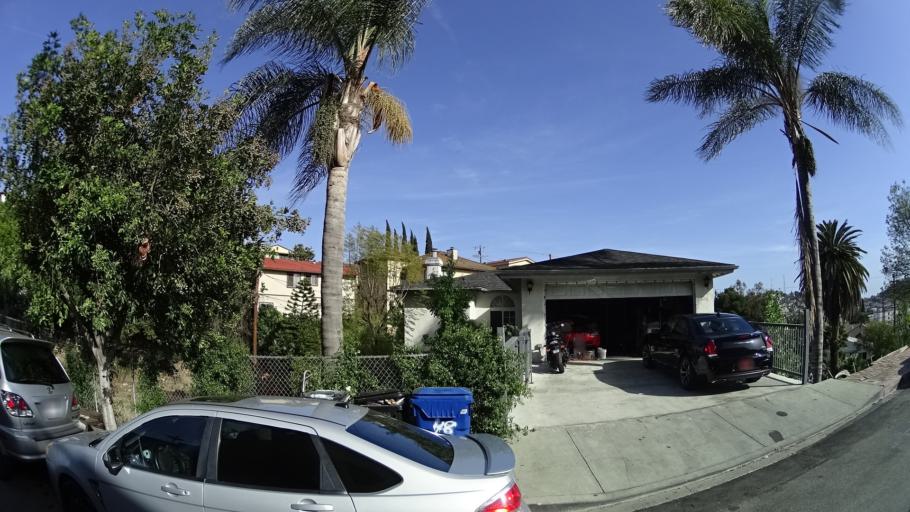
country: US
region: California
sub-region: Los Angeles County
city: Belvedere
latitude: 34.0640
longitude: -118.1762
